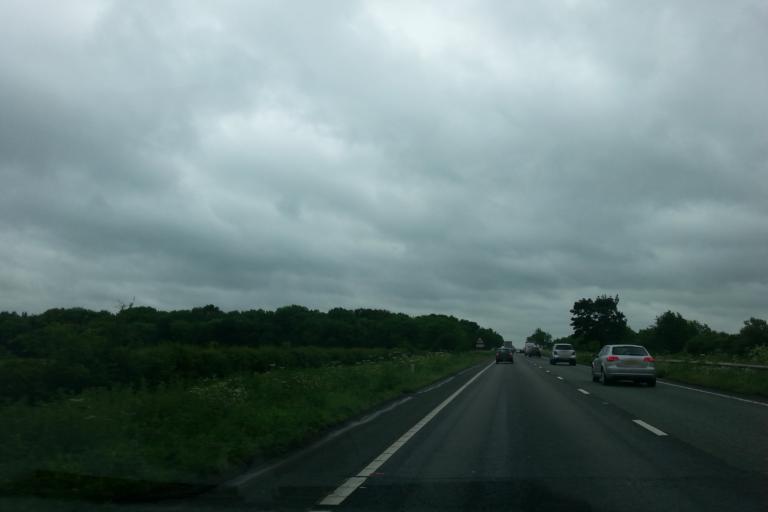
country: GB
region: England
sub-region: District of Rutland
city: Greetham
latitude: 52.7544
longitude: -0.6072
